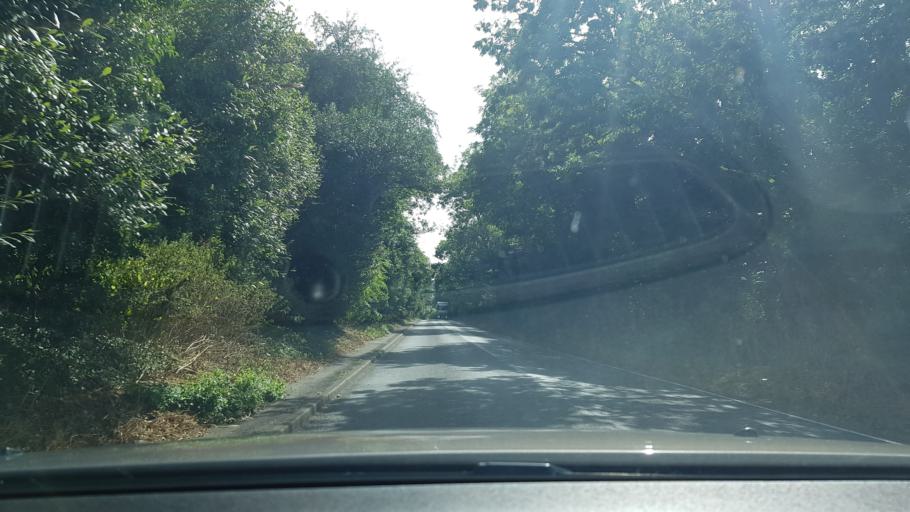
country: GB
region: England
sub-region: West Berkshire
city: Hungerford
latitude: 51.4232
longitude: -1.5035
